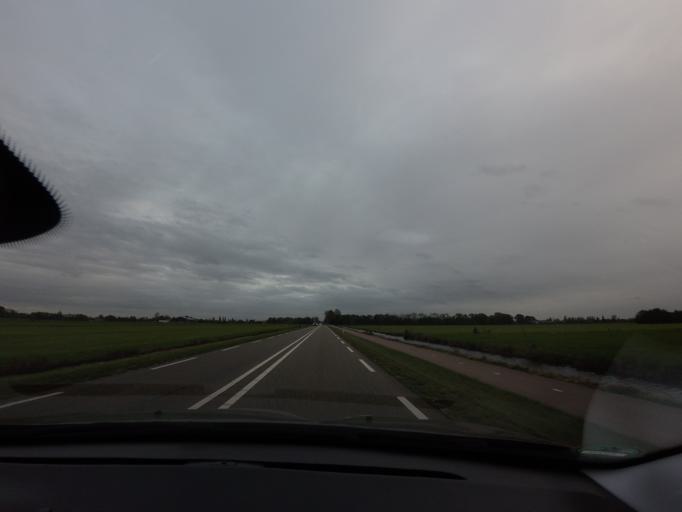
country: NL
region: Utrecht
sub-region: Gemeente Woerden
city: Woerden
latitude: 52.1370
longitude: 4.9119
